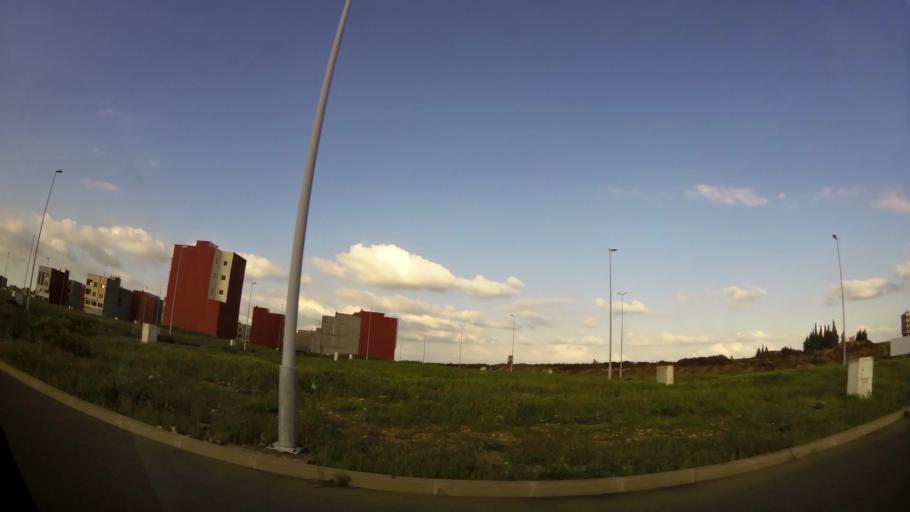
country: MA
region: Chaouia-Ouardigha
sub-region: Settat Province
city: Settat
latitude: 32.9857
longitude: -7.6386
